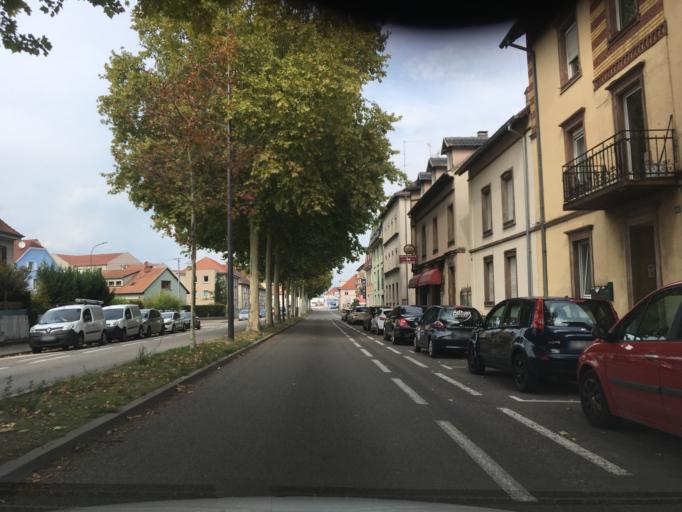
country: FR
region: Alsace
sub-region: Departement du Haut-Rhin
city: Colmar
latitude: 48.0863
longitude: 7.3610
